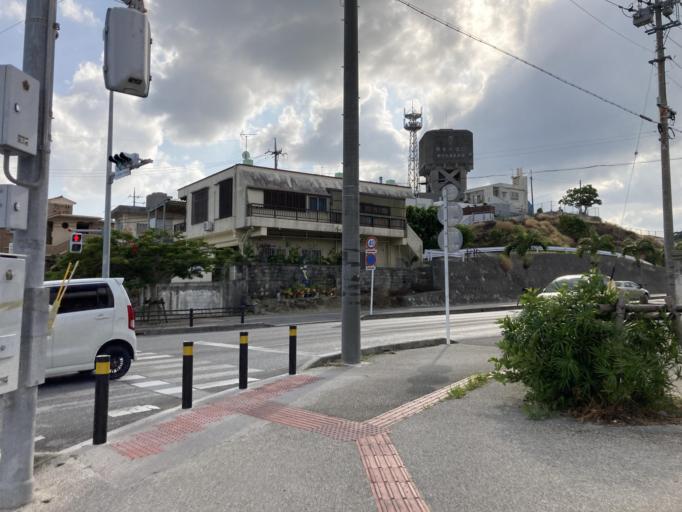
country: JP
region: Okinawa
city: Tomigusuku
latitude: 26.1553
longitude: 127.7210
